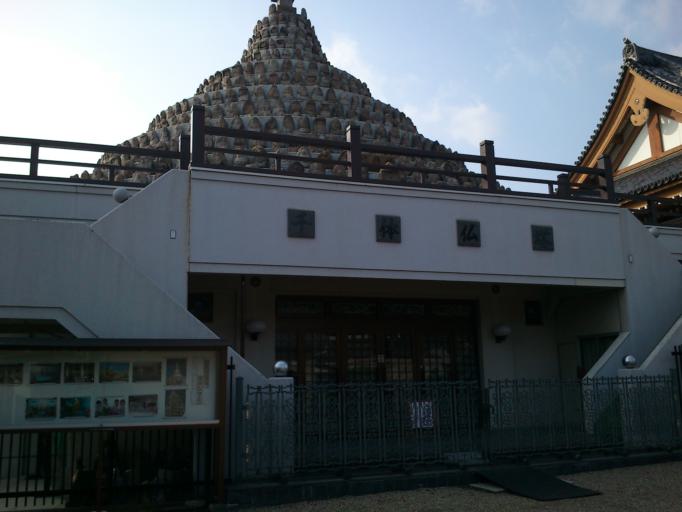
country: JP
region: Kyoto
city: Kyoto
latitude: 35.0013
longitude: 135.7435
